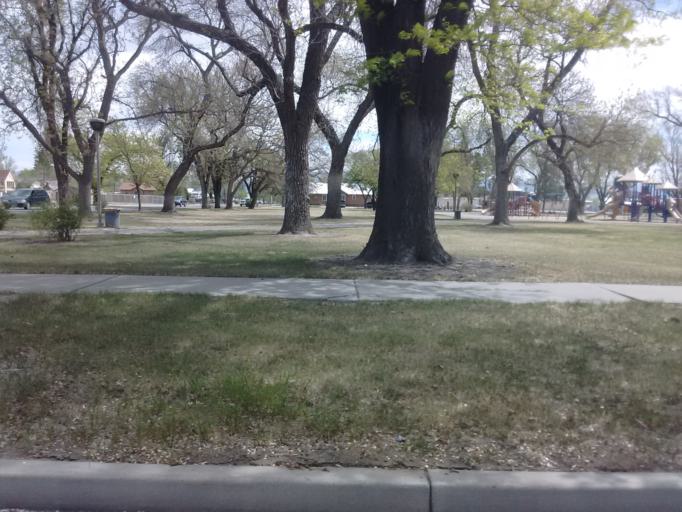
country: US
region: Colorado
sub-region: Mesa County
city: Grand Junction
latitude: 39.0651
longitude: -108.5576
